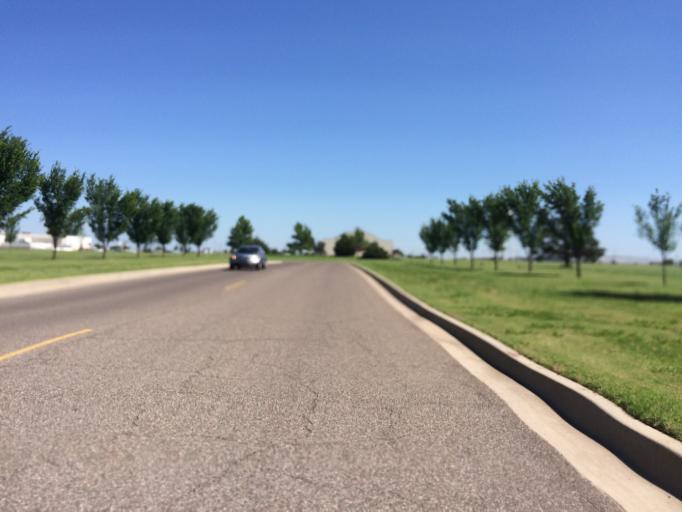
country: US
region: Oklahoma
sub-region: Cleveland County
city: Norman
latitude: 35.2369
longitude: -97.4590
